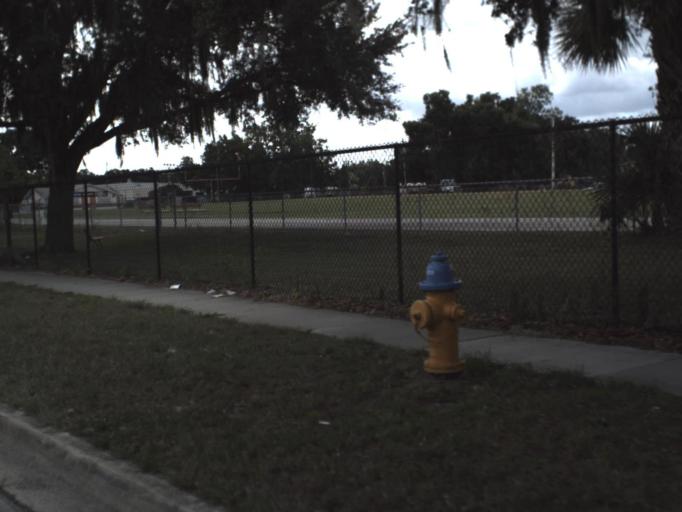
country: US
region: Florida
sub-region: Polk County
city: Lakeland
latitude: 28.0347
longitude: -81.9368
